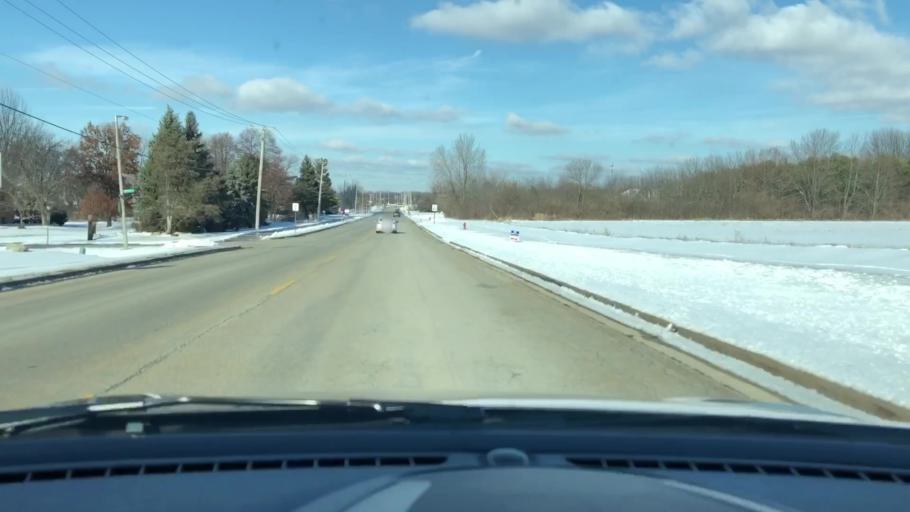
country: US
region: Illinois
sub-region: Will County
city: Mokena
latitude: 41.4939
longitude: -87.8881
